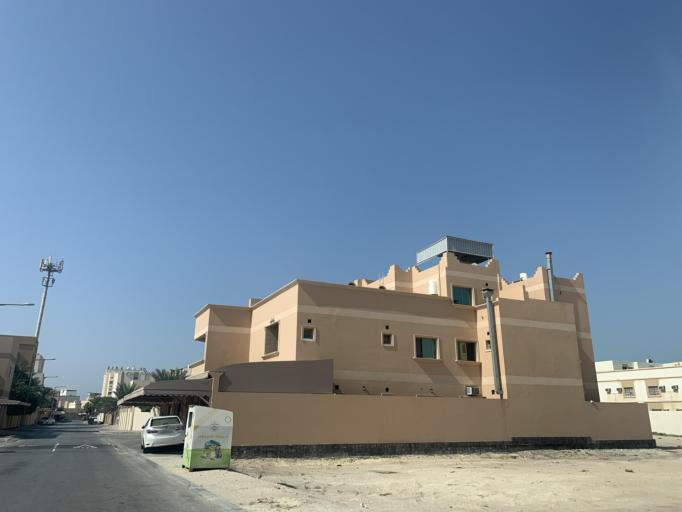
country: BH
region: Central Governorate
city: Madinat Hamad
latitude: 26.1375
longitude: 50.4958
